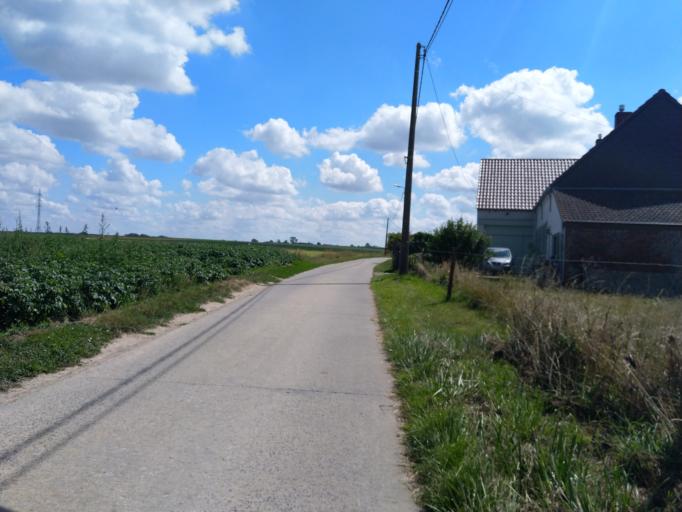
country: BE
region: Wallonia
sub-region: Province du Hainaut
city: Beloeil
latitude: 50.5458
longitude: 3.7627
